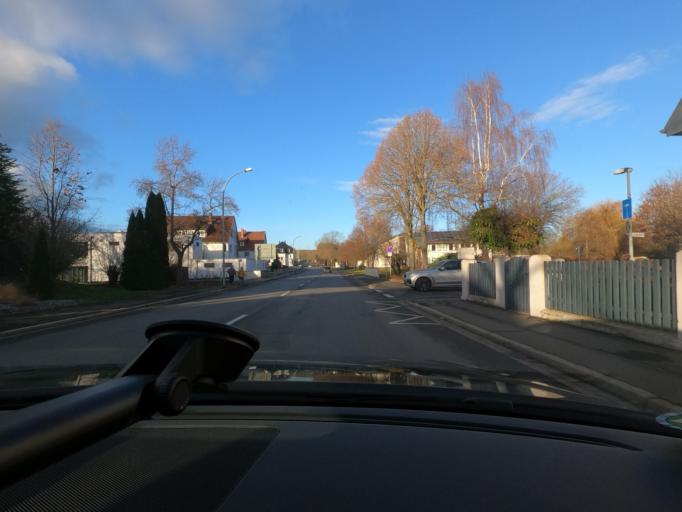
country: DE
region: Lower Saxony
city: Duderstadt
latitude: 51.5168
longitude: 10.2609
